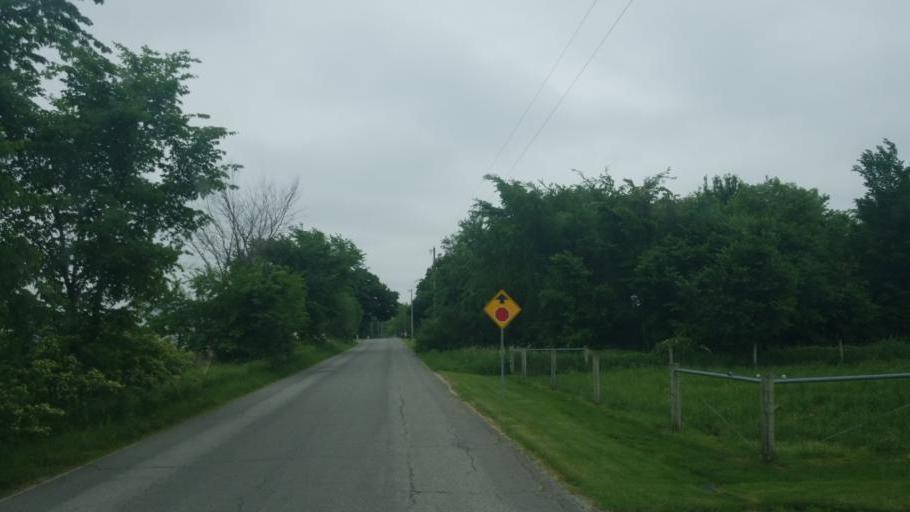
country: US
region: Indiana
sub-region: Elkhart County
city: Nappanee
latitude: 41.4718
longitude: -86.0236
